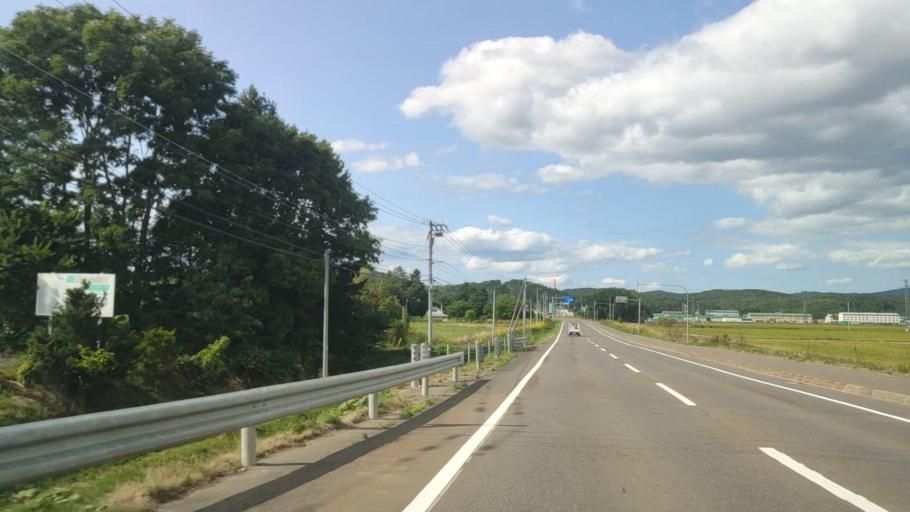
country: JP
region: Hokkaido
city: Nayoro
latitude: 44.3740
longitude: 142.4361
